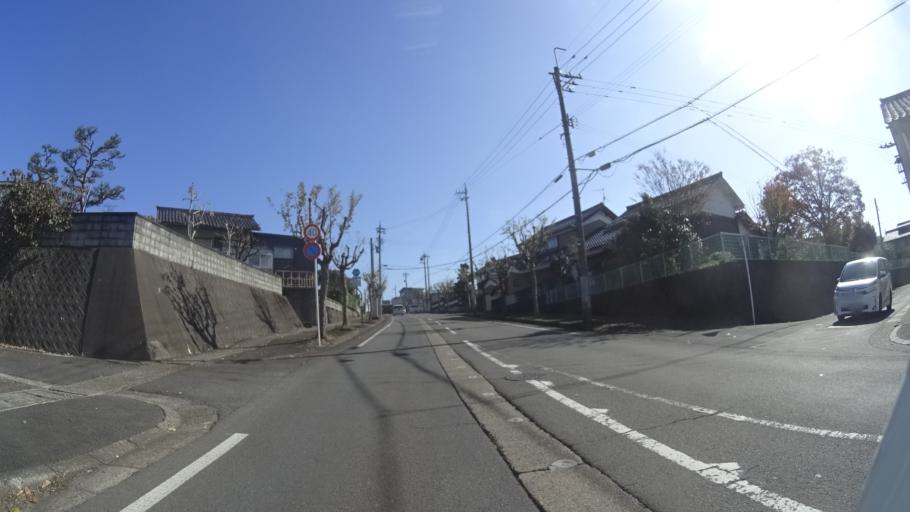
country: JP
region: Fukui
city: Sabae
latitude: 35.9638
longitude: 136.1764
